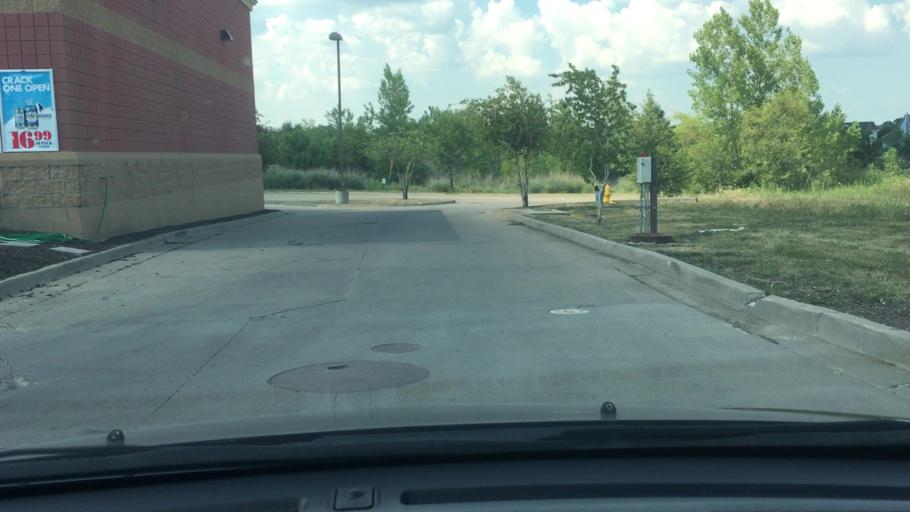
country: US
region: Missouri
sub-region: Cass County
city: Lake Winnebago
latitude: 38.8539
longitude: -94.4040
